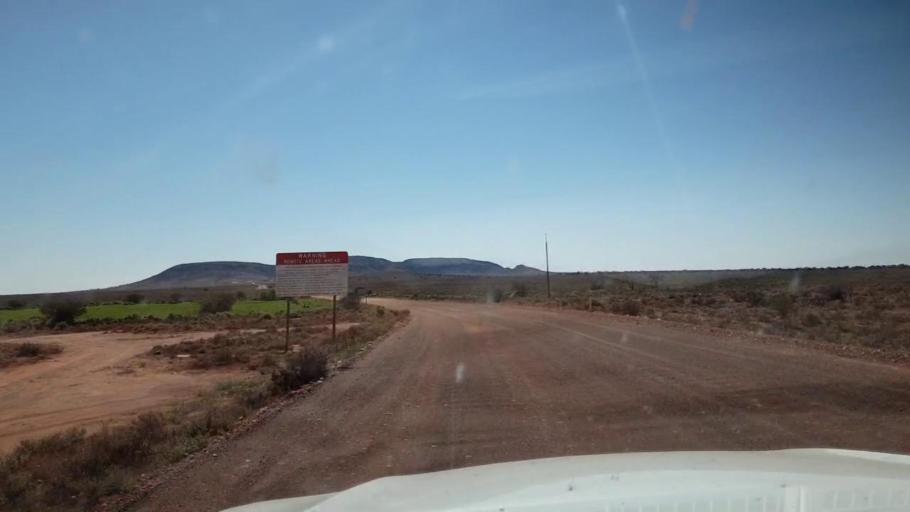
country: AU
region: South Australia
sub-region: Whyalla
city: Whyalla
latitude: -32.7166
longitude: 137.1434
